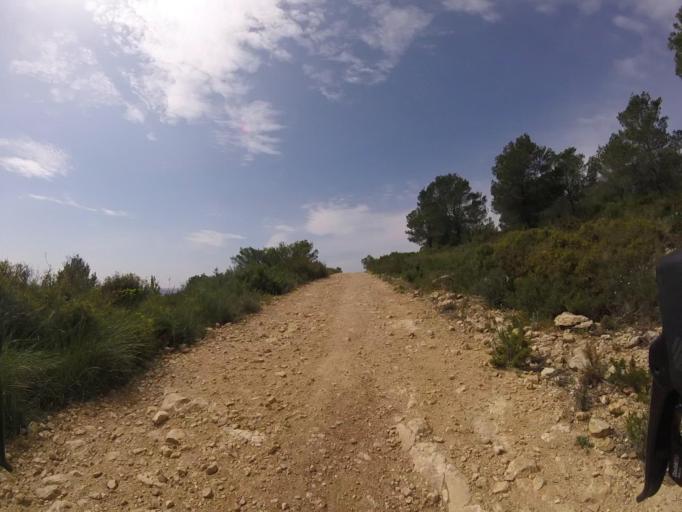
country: ES
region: Valencia
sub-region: Provincia de Castello
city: Cuevas de Vinroma
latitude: 40.2773
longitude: 0.1220
